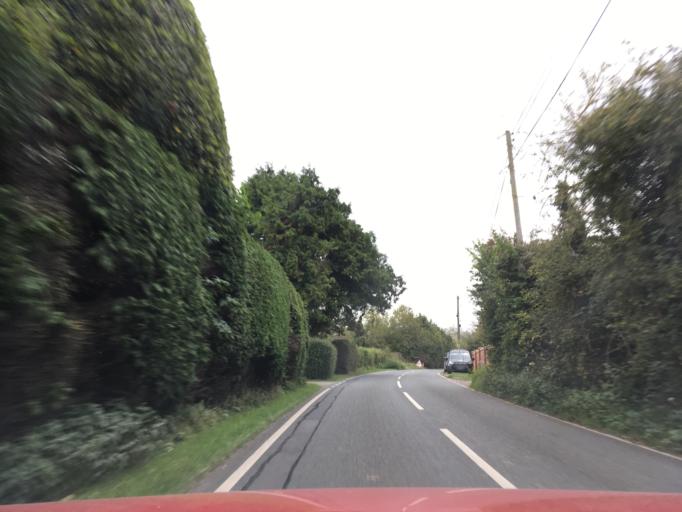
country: GB
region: England
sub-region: Gloucestershire
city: Stonehouse
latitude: 51.7594
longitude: -2.3148
